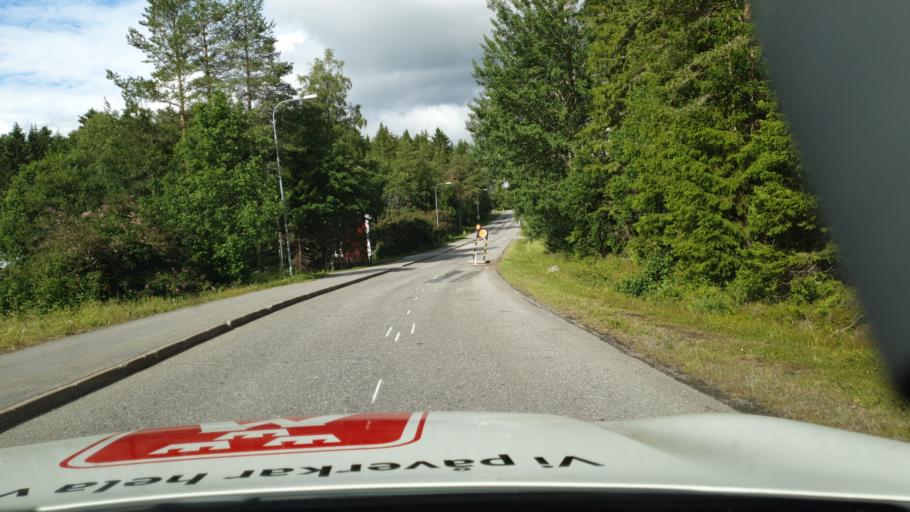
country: SE
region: Vaesterbotten
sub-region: Umea Kommun
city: Hoernefors
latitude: 63.6808
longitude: 20.0162
